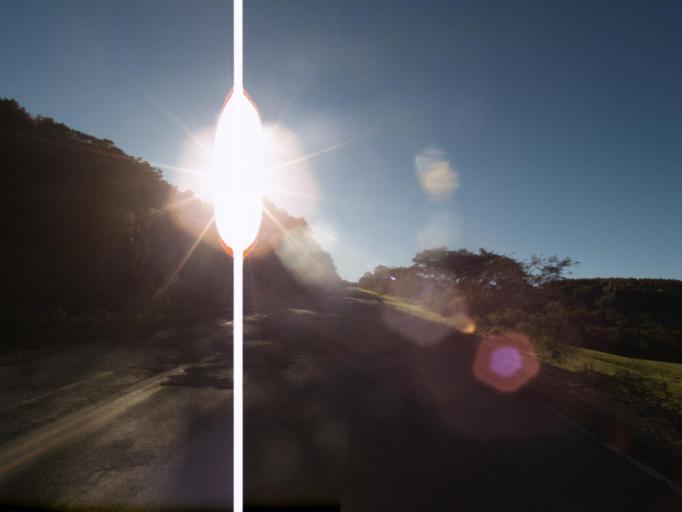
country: AR
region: Misiones
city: Bernardo de Irigoyen
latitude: -26.3269
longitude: -53.5463
